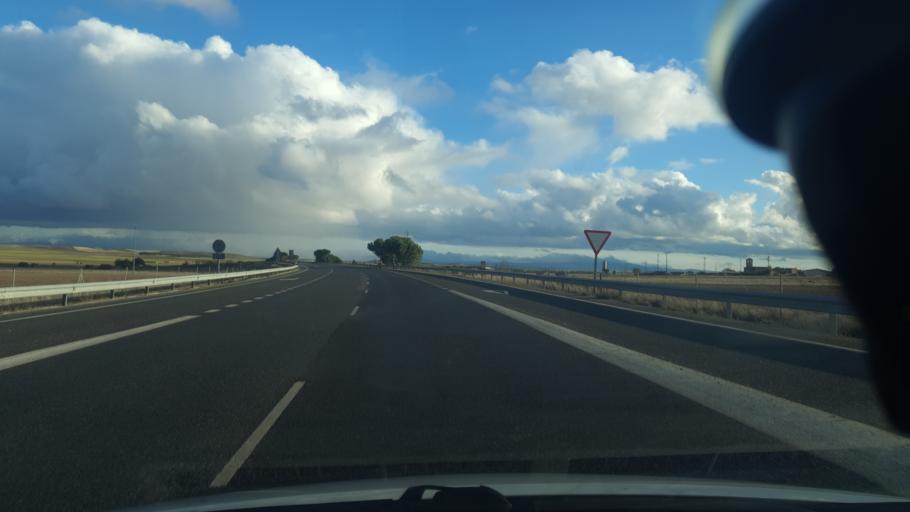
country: ES
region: Castille and Leon
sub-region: Provincia de Segovia
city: Codorniz
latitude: 41.0539
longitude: -4.6285
